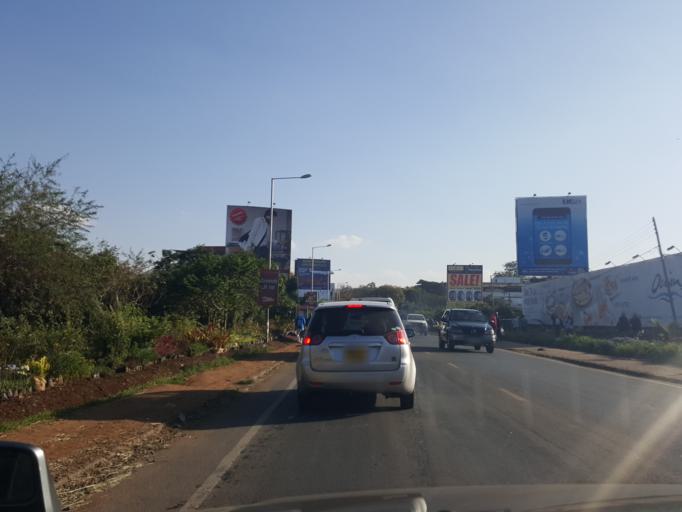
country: KE
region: Nairobi Area
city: Nairobi
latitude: -1.2767
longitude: 36.7712
